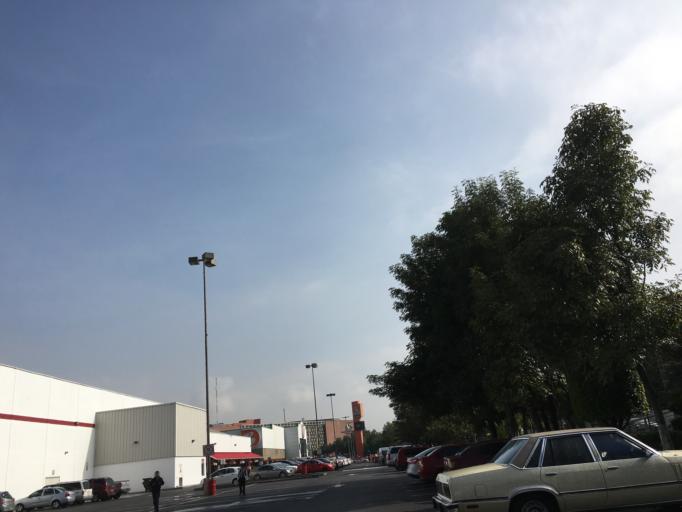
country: MX
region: Mexico City
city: Tlalpan
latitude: 19.2837
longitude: -99.1383
